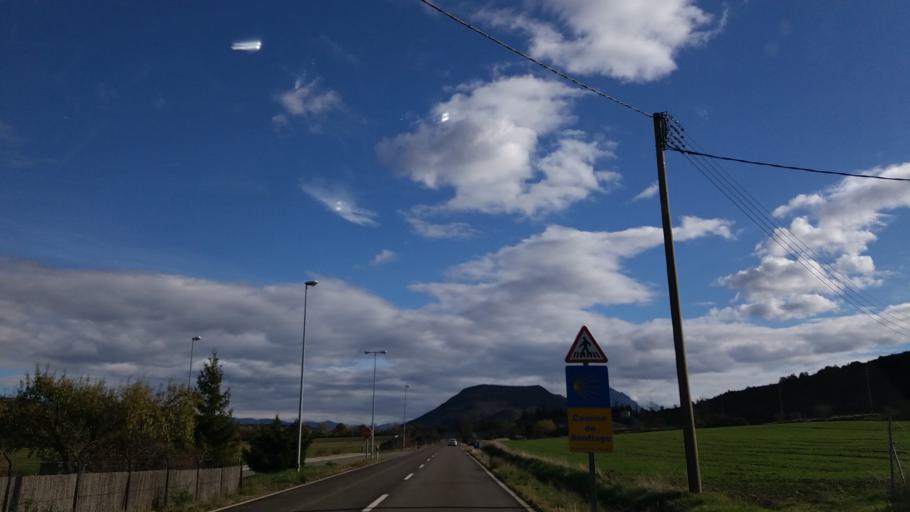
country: ES
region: Aragon
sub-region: Provincia de Huesca
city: Santa Cruz de la Seros
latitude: 42.5578
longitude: -0.7121
